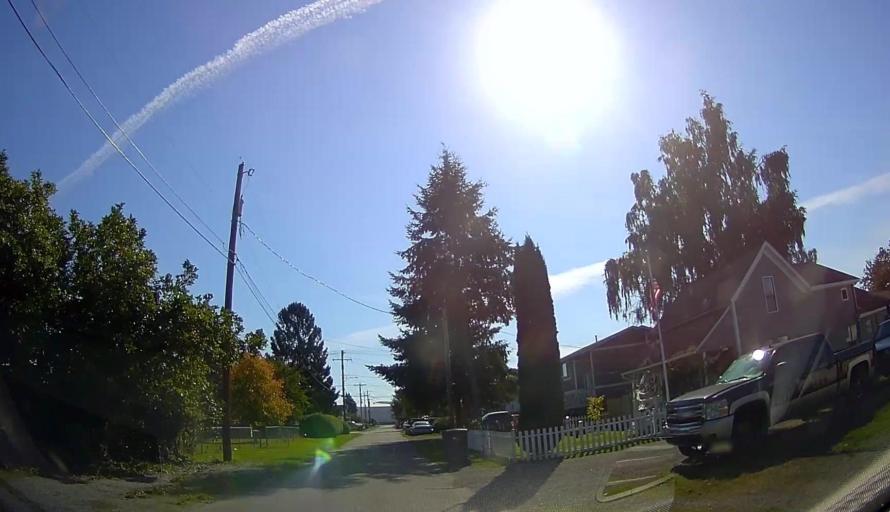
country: US
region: Washington
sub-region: Snohomish County
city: Stanwood
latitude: 48.2431
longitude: -122.3730
